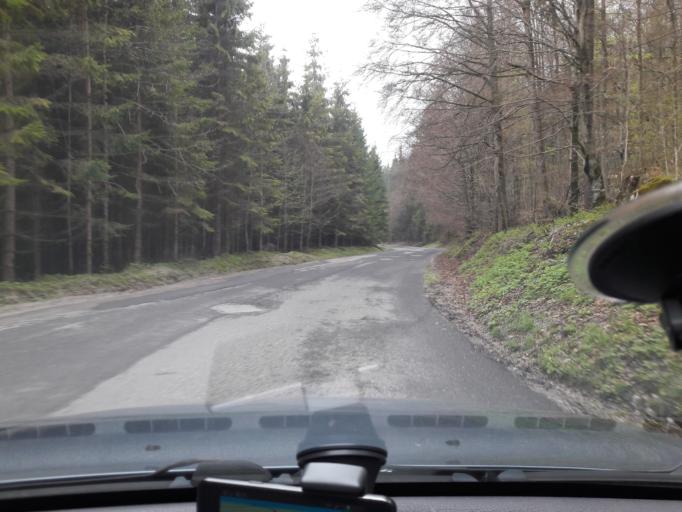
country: SK
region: Banskobystricky
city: Revuca
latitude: 48.7952
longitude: 20.1340
